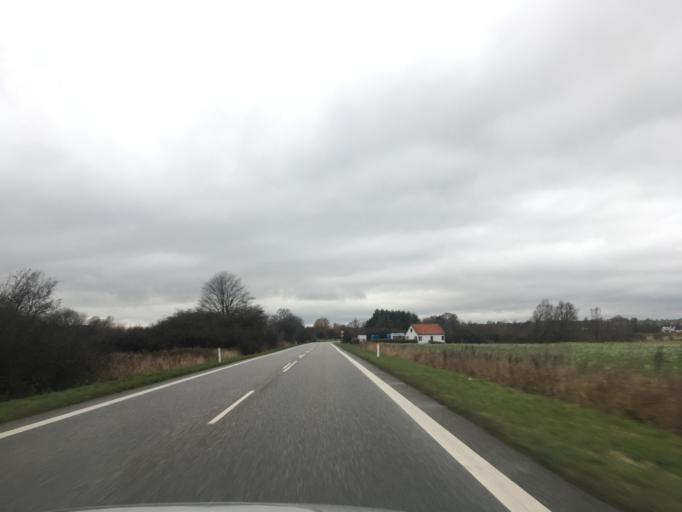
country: DK
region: Zealand
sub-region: Holbaek Kommune
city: Holbaek
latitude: 55.7194
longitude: 11.6431
